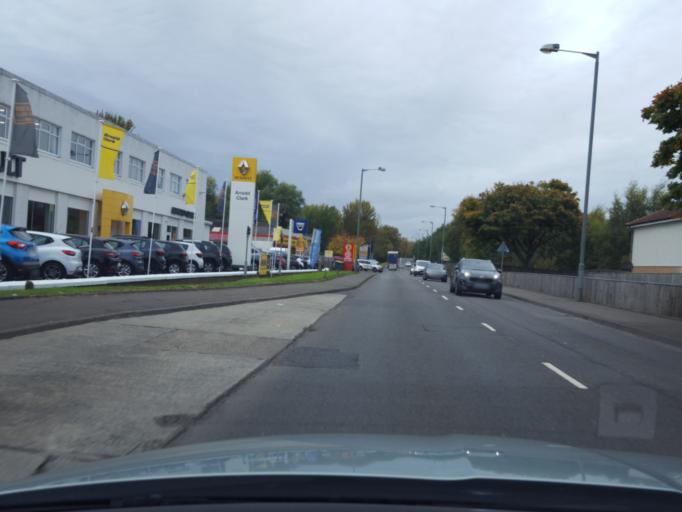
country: GB
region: Scotland
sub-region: Falkirk
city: Grangemouth
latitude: 56.0067
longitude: -3.7363
